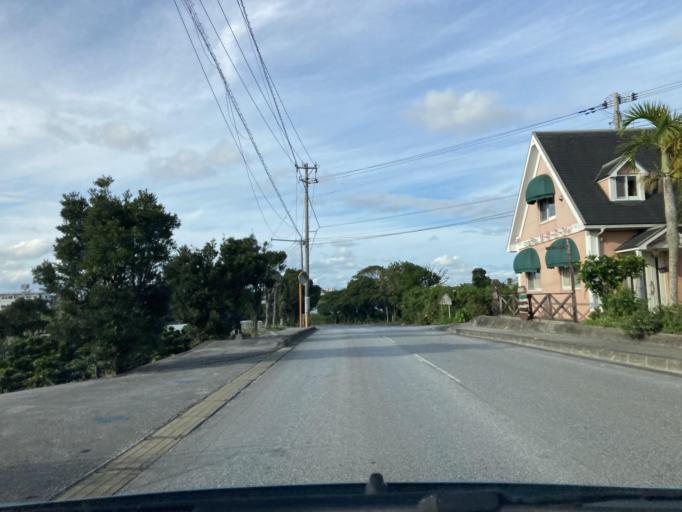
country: JP
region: Okinawa
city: Tomigusuku
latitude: 26.1497
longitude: 127.7448
